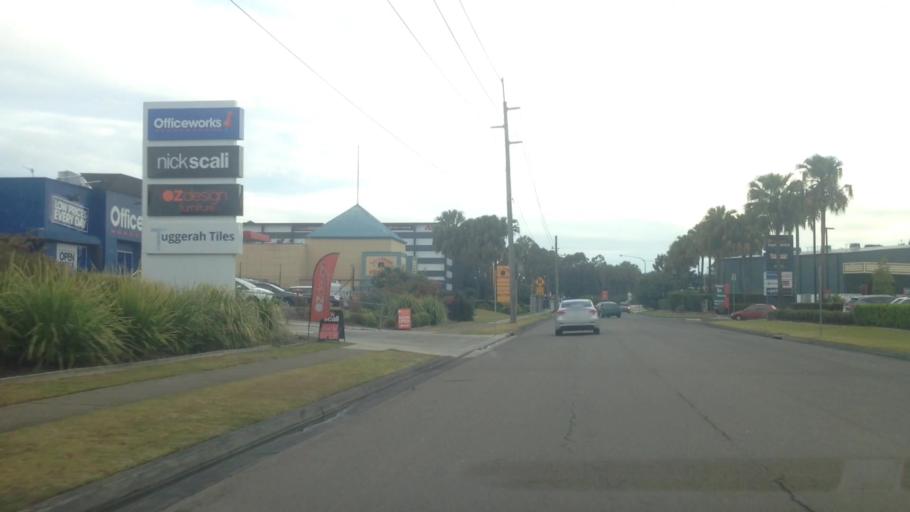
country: AU
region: New South Wales
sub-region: Wyong Shire
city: Chittaway Bay
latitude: -33.3105
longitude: 151.4226
